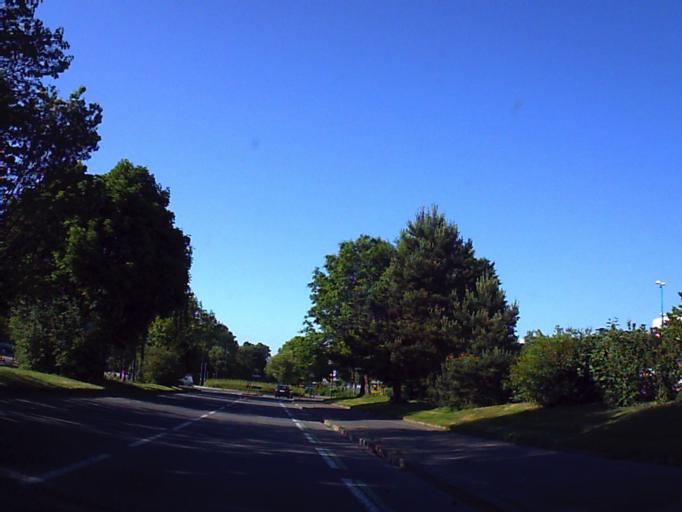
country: FR
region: Brittany
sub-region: Departement d'Ille-et-Vilaine
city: Rennes
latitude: 48.1332
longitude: -1.6521
